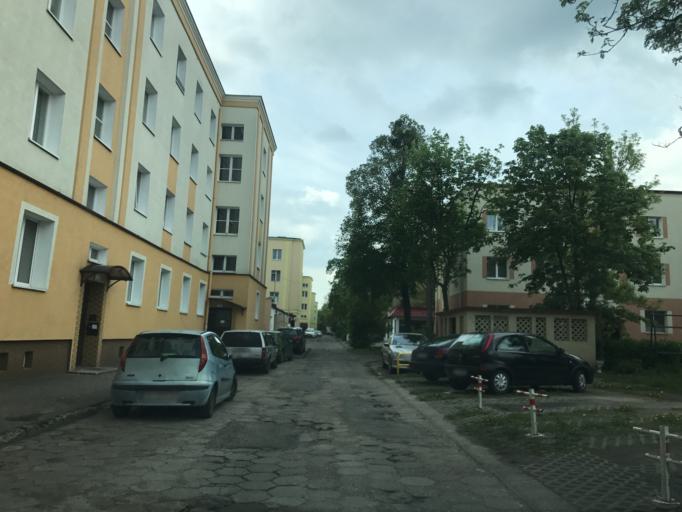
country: PL
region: Kujawsko-Pomorskie
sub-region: Bydgoszcz
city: Bydgoszcz
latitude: 53.1413
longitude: 18.0285
